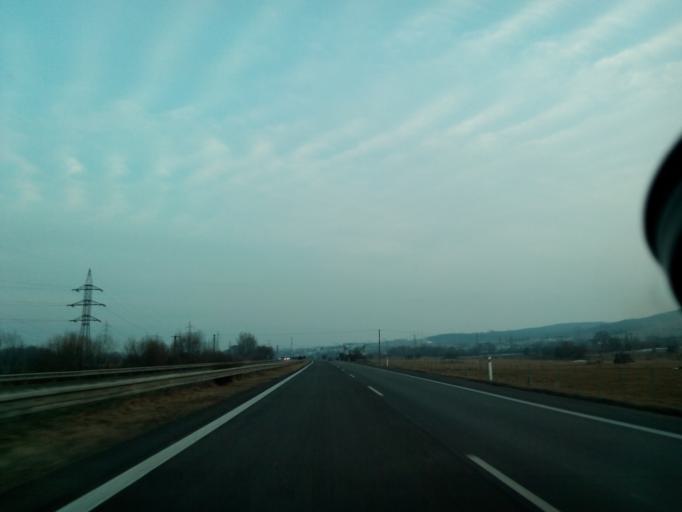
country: SK
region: Presovsky
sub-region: Okres Presov
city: Presov
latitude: 48.8727
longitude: 21.2540
